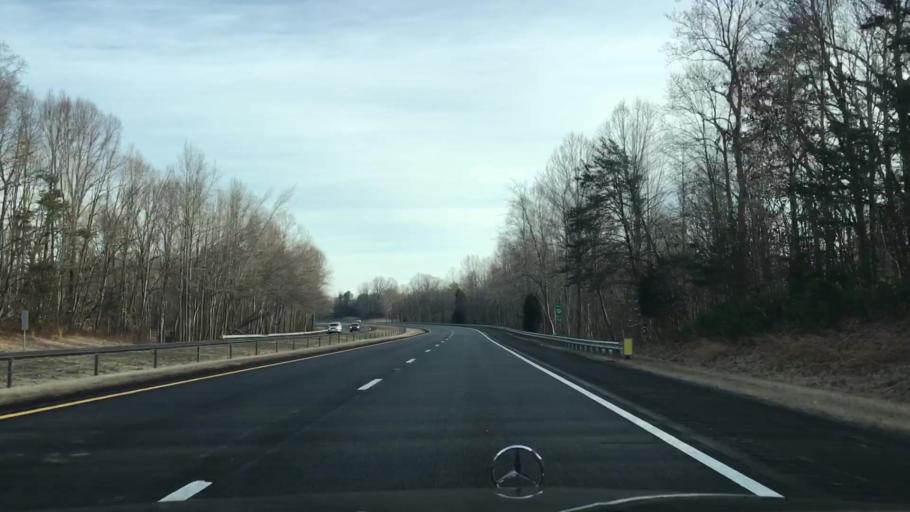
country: US
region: North Carolina
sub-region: Rockingham County
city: Reidsville
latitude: 36.4222
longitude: -79.5772
